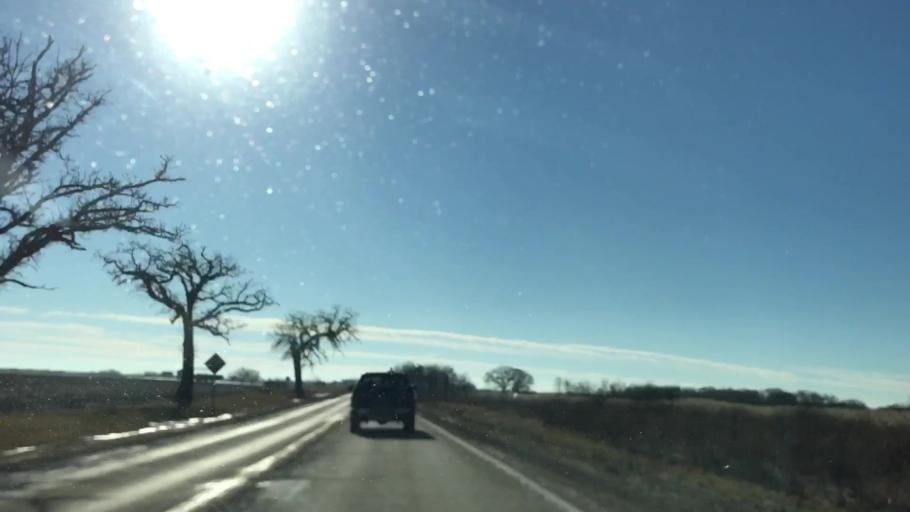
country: US
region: Illinois
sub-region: Kane County
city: Pingree Grove
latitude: 42.1029
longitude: -88.4548
